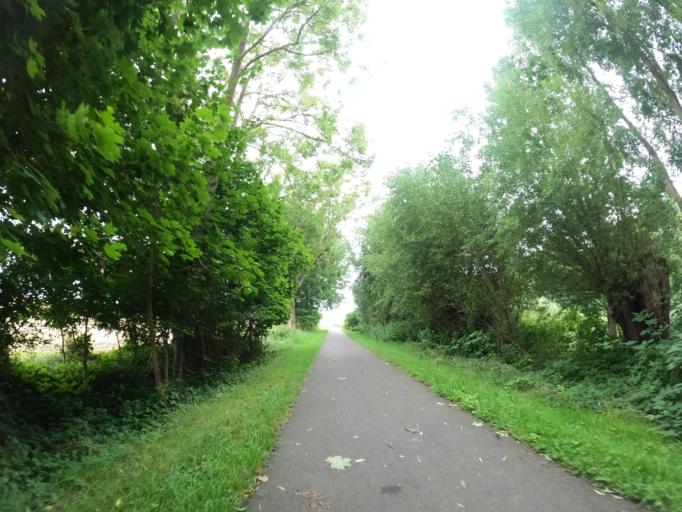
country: DE
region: Mecklenburg-Vorpommern
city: Poseritz
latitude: 54.2951
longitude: 13.2768
